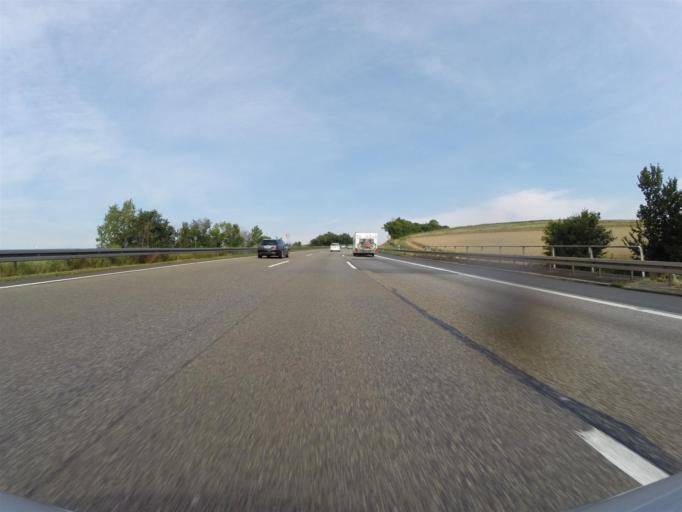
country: DE
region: Hesse
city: Schwarzenborn
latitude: 50.9380
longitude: 9.5422
